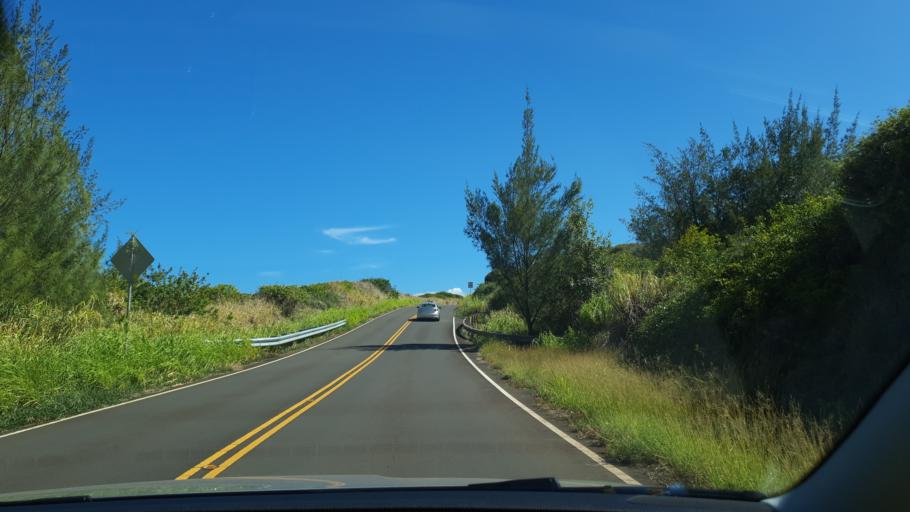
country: US
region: Hawaii
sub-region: Maui County
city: Napili-Honokowai
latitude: 21.0158
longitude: -156.5756
